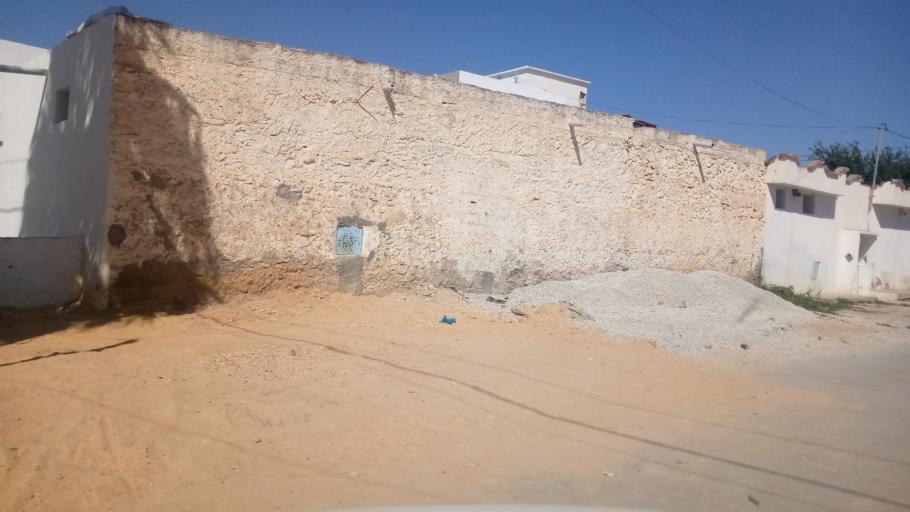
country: TN
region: Al Qayrawan
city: Sbikha
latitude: 36.1192
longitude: 10.0932
